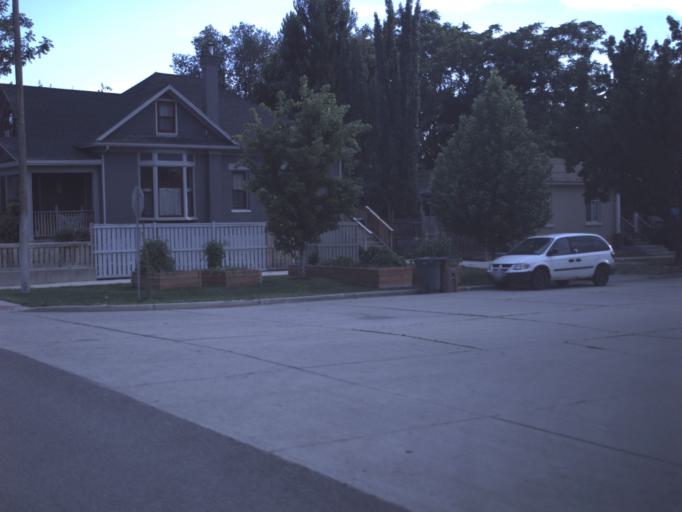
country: US
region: Utah
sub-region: Salt Lake County
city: Salt Lake City
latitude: 40.7781
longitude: -111.8998
